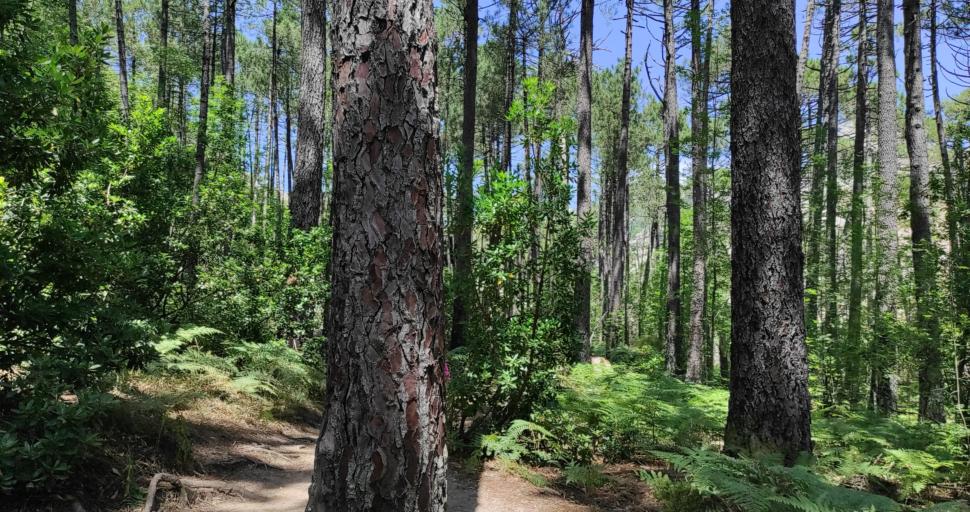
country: FR
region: Corsica
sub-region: Departement de la Corse-du-Sud
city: Zonza
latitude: 41.6846
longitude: 9.2026
